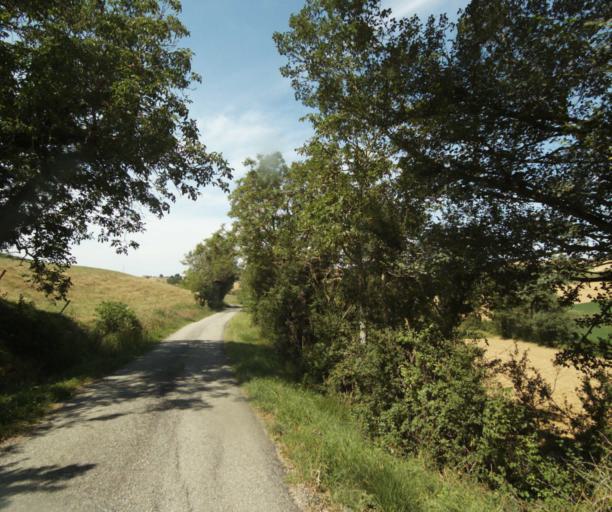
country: FR
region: Midi-Pyrenees
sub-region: Departement de l'Ariege
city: Lezat-sur-Leze
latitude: 43.2547
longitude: 1.4053
